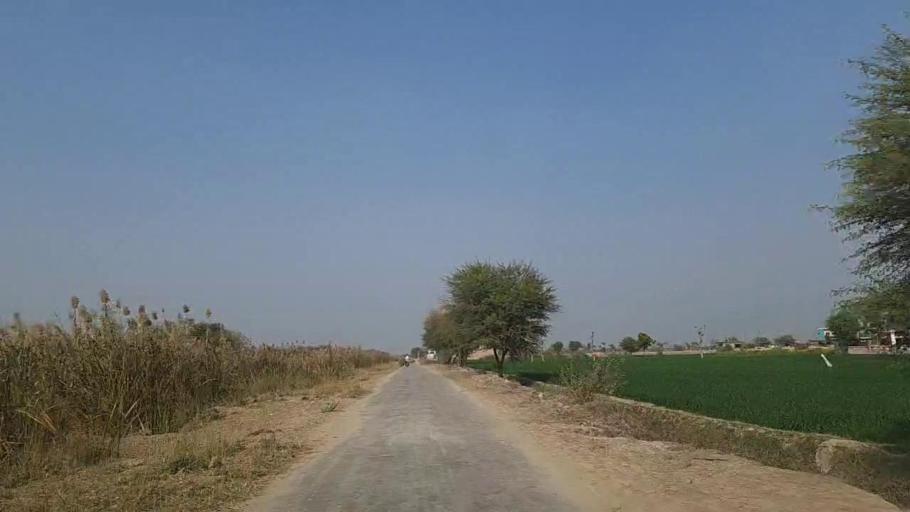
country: PK
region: Sindh
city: Daur
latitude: 26.4724
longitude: 68.4663
